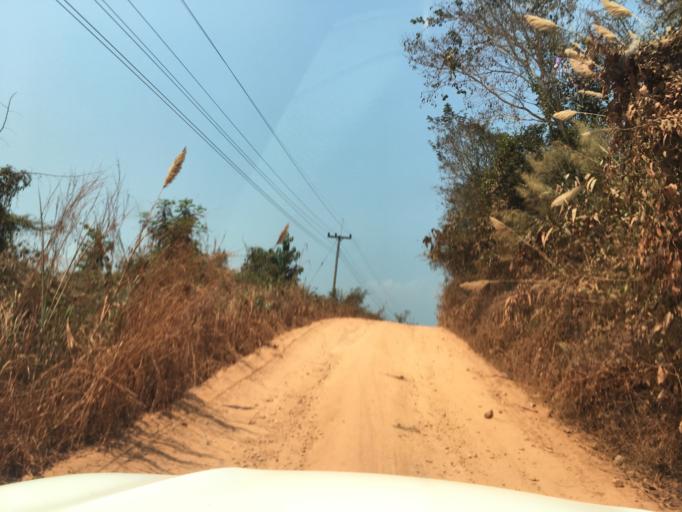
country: LA
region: Bolikhamxai
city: Bolikhan
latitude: 18.7381
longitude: 103.6250
